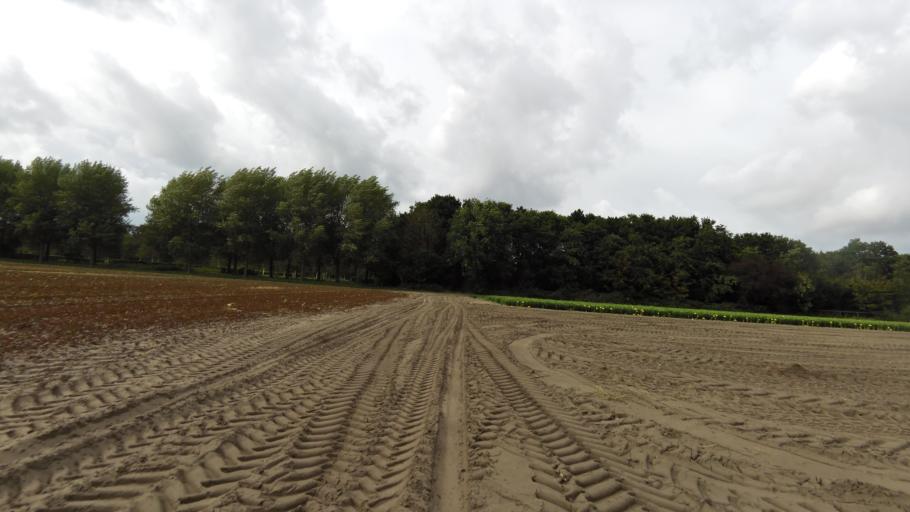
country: NL
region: South Holland
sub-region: Gemeente Noordwijk
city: Noordwijk-Binnen
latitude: 52.2380
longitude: 4.4598
